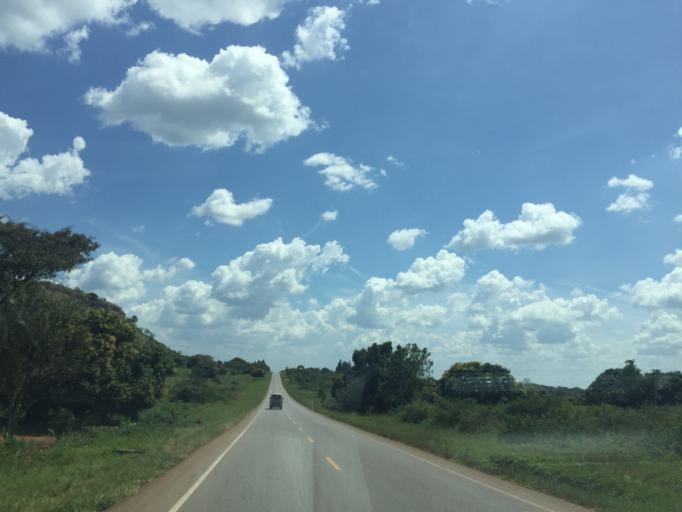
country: UG
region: Central Region
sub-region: Nakasongola District
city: Nakasongola
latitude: 1.3172
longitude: 32.4221
